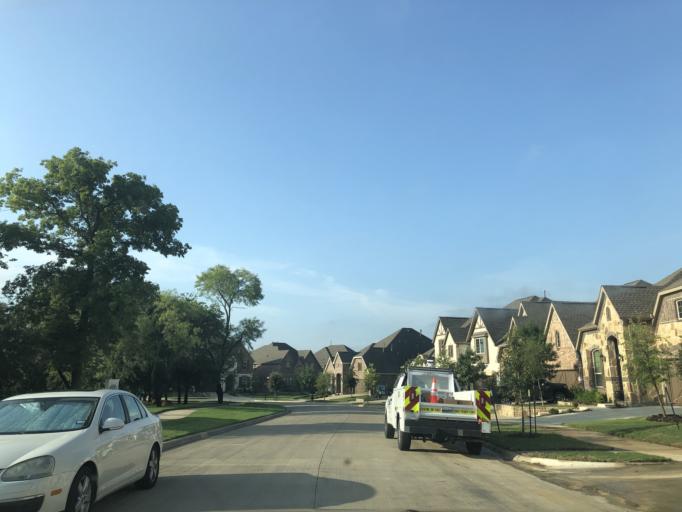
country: US
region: Texas
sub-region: Tarrant County
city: Euless
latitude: 32.8500
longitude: -97.0676
